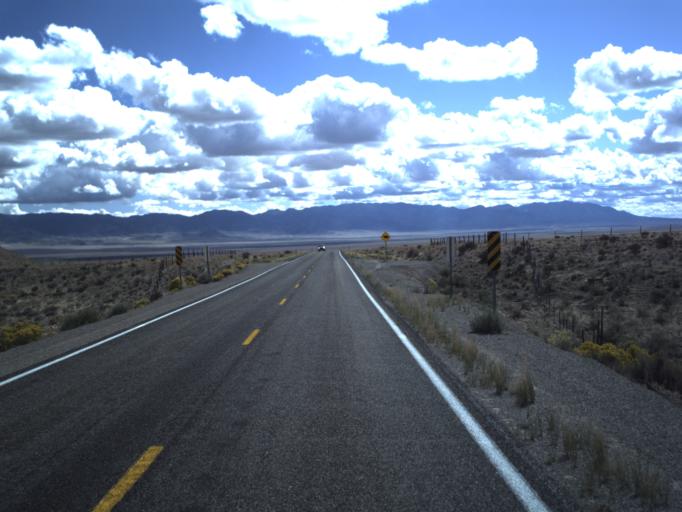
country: US
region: Utah
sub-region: Beaver County
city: Milford
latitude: 38.5892
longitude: -113.8181
